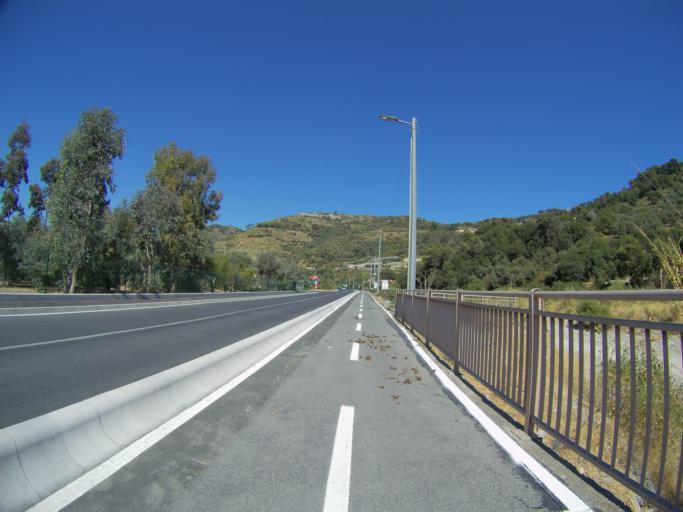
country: IT
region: Liguria
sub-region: Provincia di Imperia
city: Camporosso
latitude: 43.8112
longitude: 7.6297
